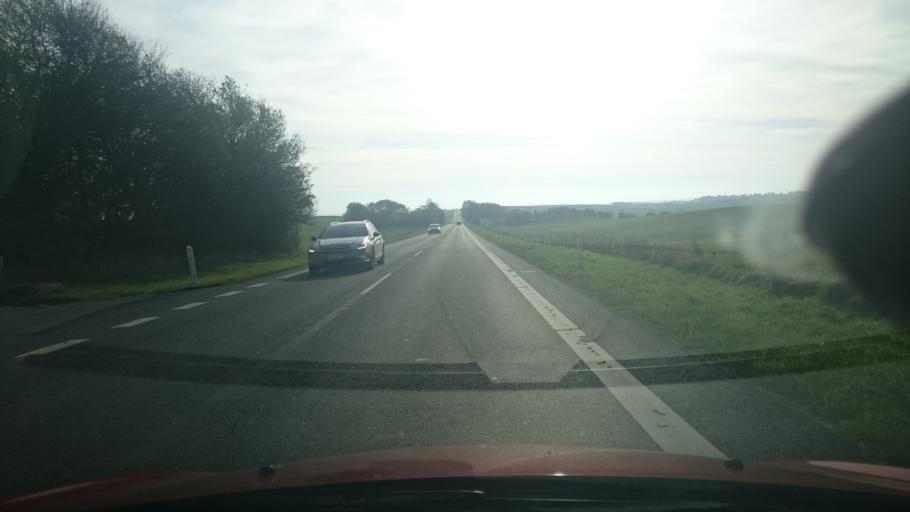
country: DK
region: Central Jutland
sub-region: Randers Kommune
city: Assentoft
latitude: 56.4338
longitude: 10.1892
